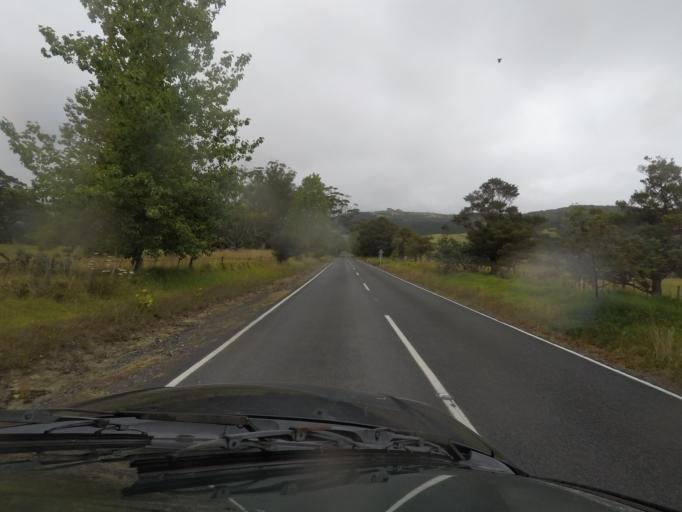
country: NZ
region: Auckland
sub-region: Auckland
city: Warkworth
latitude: -36.2629
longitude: 174.7041
